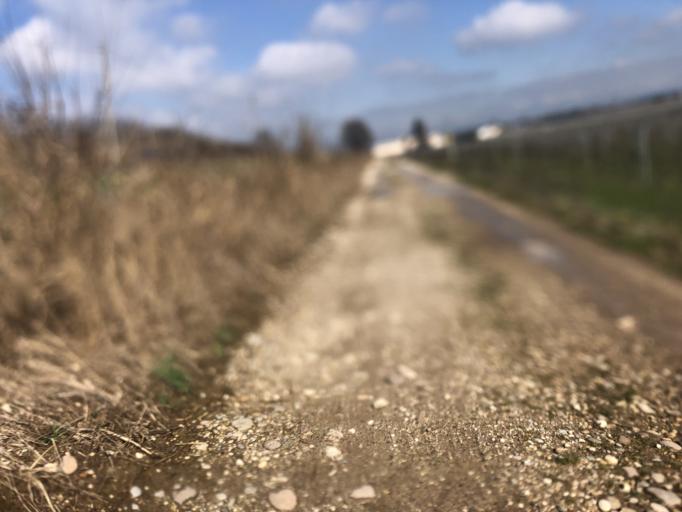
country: IT
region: Veneto
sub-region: Provincia di Verona
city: San Giorgio in Salici
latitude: 45.4112
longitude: 10.7918
